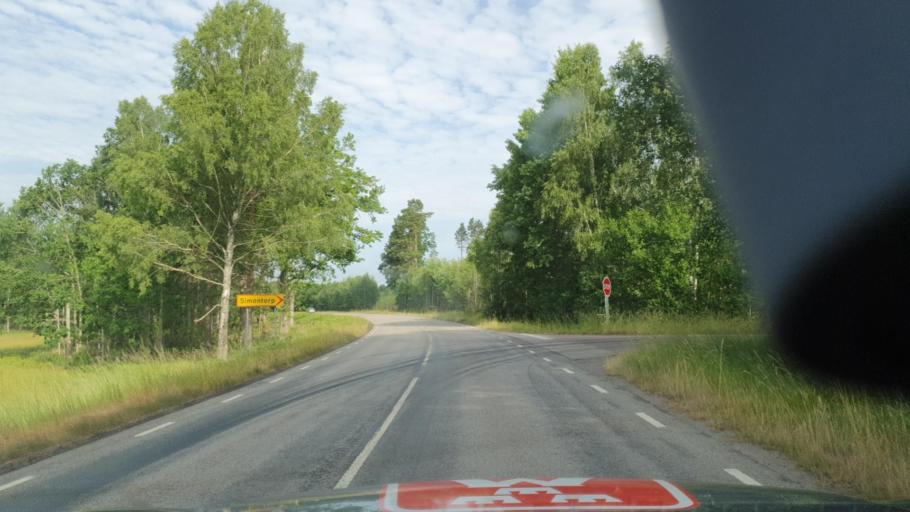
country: SE
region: Kalmar
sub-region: Nybro Kommun
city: Nybro
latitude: 56.7222
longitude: 15.9712
